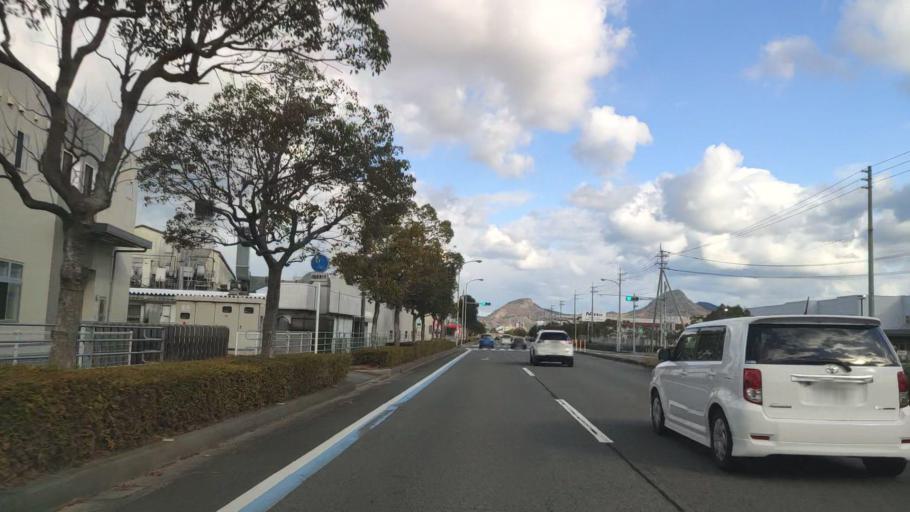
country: JP
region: Ehime
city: Hojo
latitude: 33.9591
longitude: 132.7770
